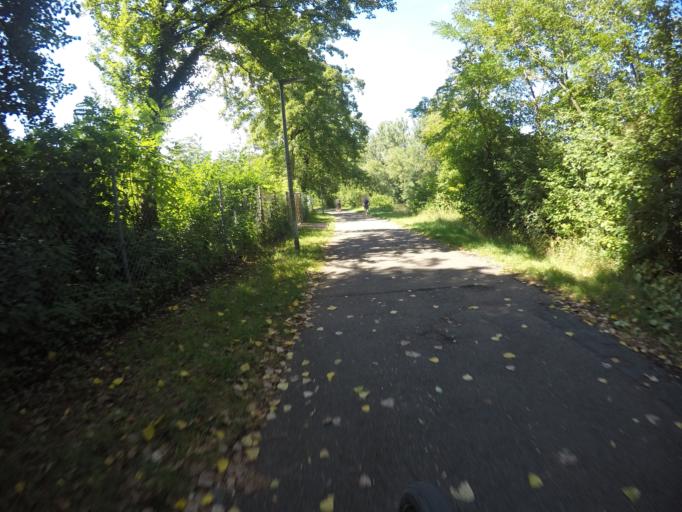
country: DE
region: Baden-Wuerttemberg
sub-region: Regierungsbezirk Stuttgart
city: Esslingen
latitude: 48.7256
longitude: 9.3297
